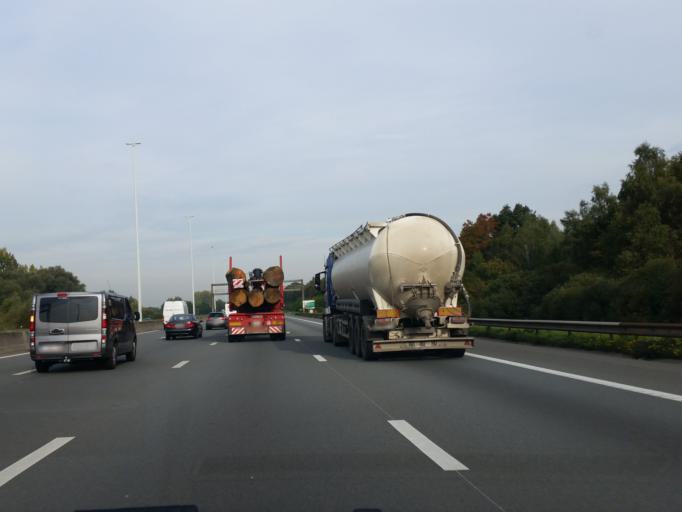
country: BE
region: Flanders
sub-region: Provincie Antwerpen
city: Edegem
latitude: 51.1469
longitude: 4.4254
